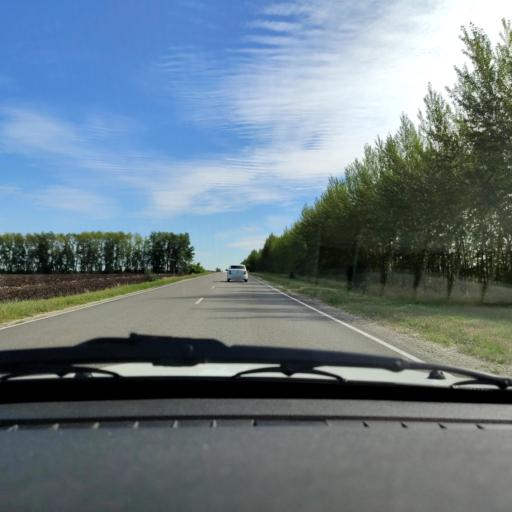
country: RU
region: Voronezj
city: Volya
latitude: 51.7246
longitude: 39.5490
